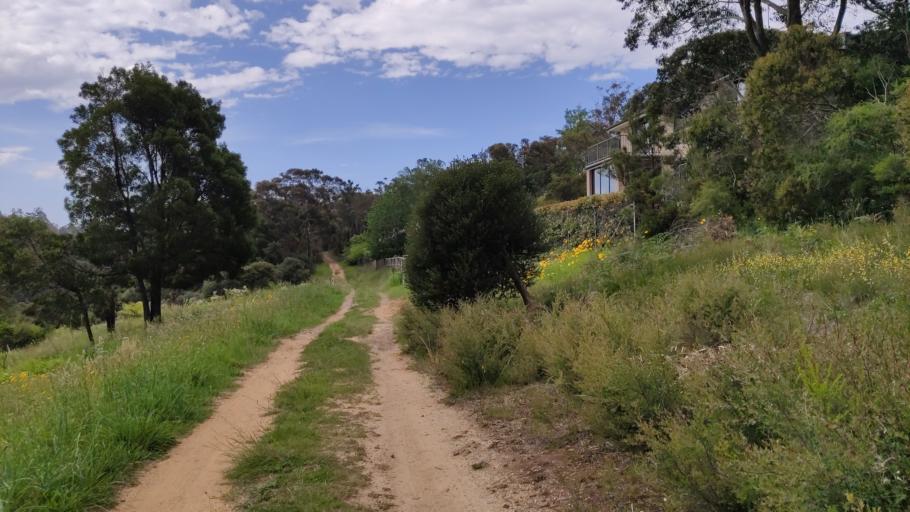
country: AU
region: New South Wales
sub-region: Blue Mountains Municipality
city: Leura
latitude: -33.7184
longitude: 150.3266
